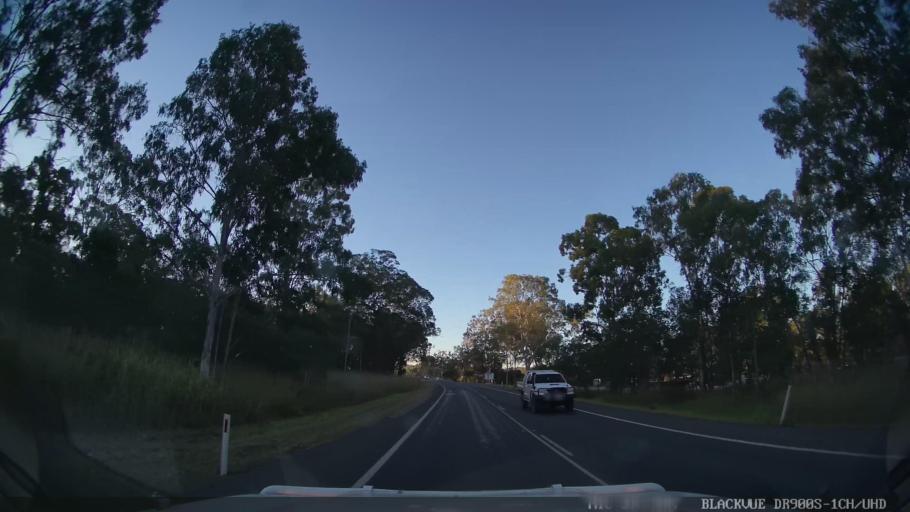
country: AU
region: Queensland
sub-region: Gladstone
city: Toolooa
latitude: -23.9569
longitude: 151.2198
